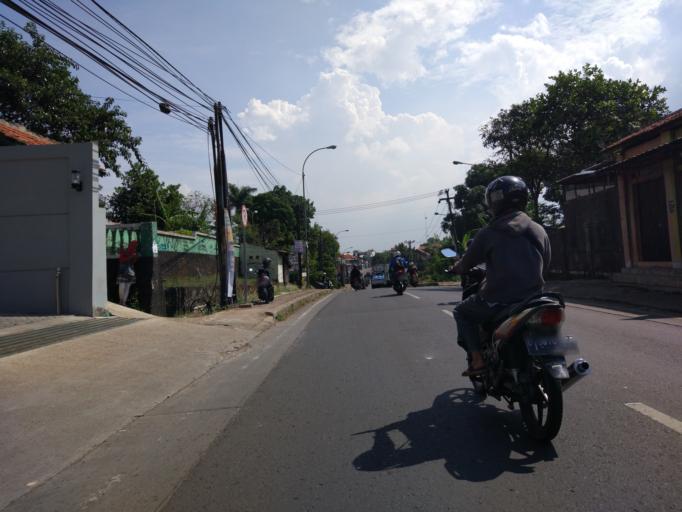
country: ID
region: West Java
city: Cileunyi
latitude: -6.9408
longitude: 107.7442
